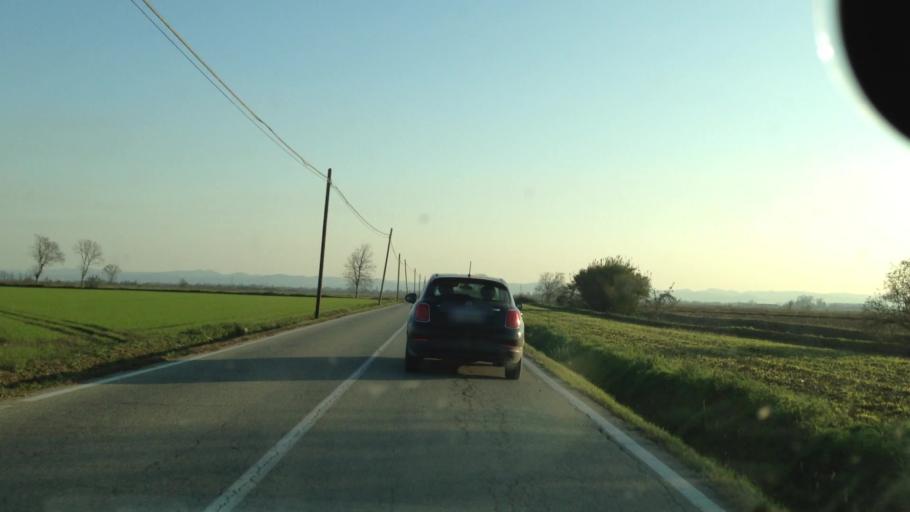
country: IT
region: Piedmont
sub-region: Provincia di Vercelli
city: Livorno Ferraris
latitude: 45.2699
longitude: 8.0821
